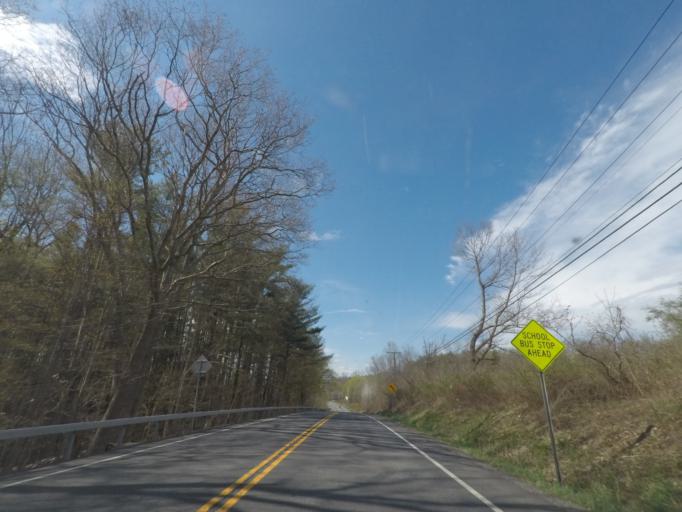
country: US
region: New York
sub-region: Greene County
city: Cairo
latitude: 42.3332
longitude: -74.0201
